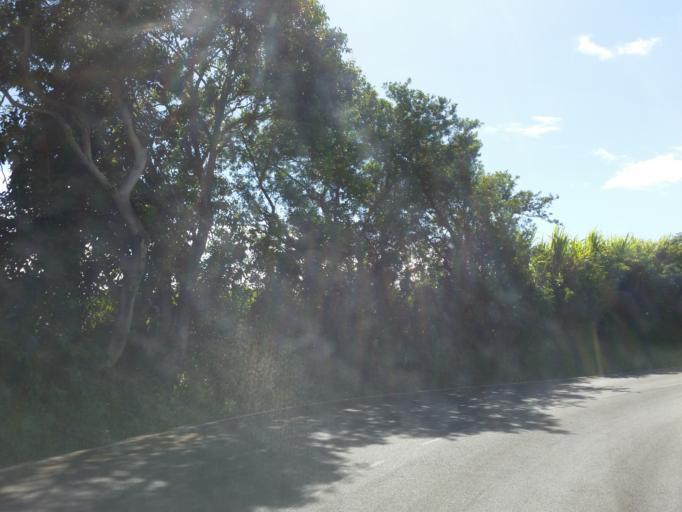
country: RE
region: Reunion
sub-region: Reunion
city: Sainte-Marie
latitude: -20.9158
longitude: 55.5372
